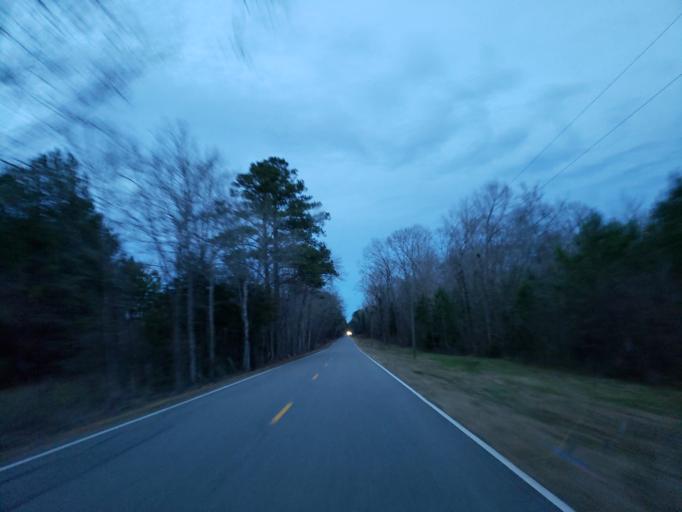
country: US
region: Alabama
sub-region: Greene County
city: Eutaw
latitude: 32.8816
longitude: -88.0668
